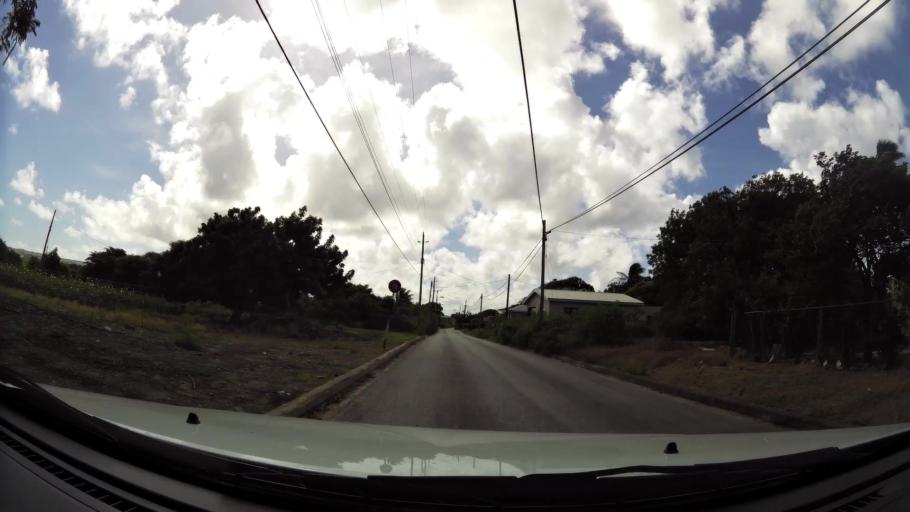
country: BB
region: Saint Lucy
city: Checker Hall
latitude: 13.2895
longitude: -59.6408
